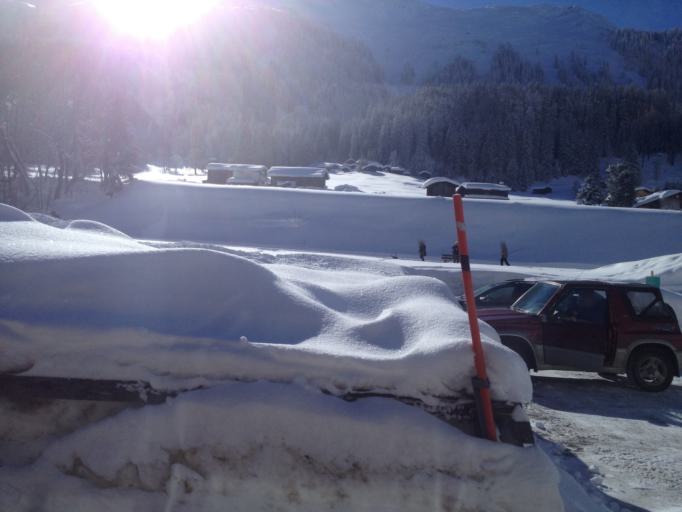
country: CH
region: Grisons
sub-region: Praettigau/Davos District
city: Klosters Serneus
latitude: 46.8626
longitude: 9.9076
